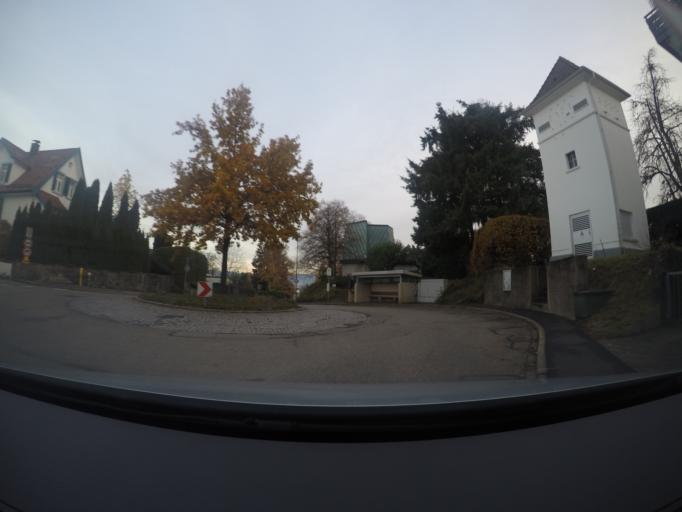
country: DE
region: Baden-Wuerttemberg
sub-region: Karlsruhe Region
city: Baden-Baden
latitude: 48.7783
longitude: 8.2709
